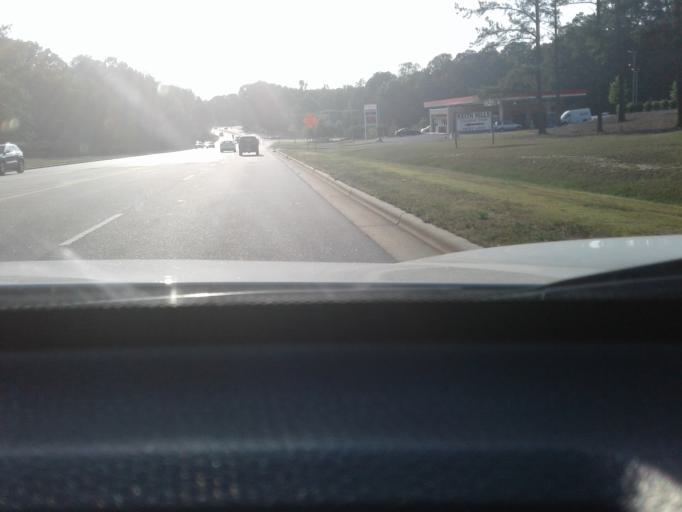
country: US
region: North Carolina
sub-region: Harnett County
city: Buies Creek
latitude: 35.4062
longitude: -78.7444
